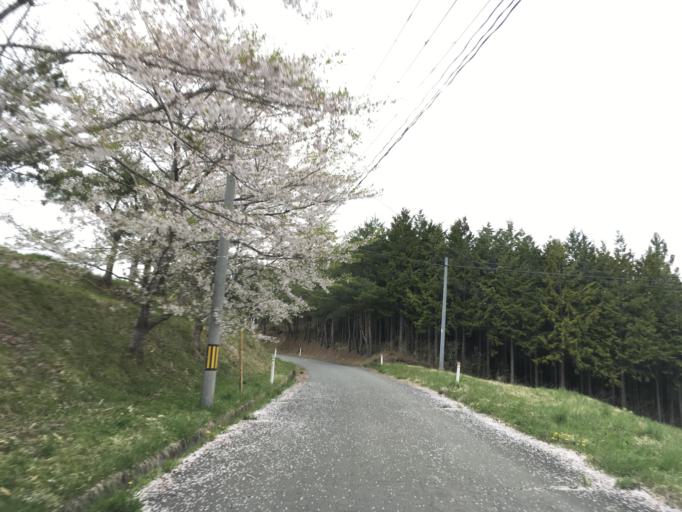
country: JP
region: Iwate
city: Ichinoseki
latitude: 38.8556
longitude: 141.3260
